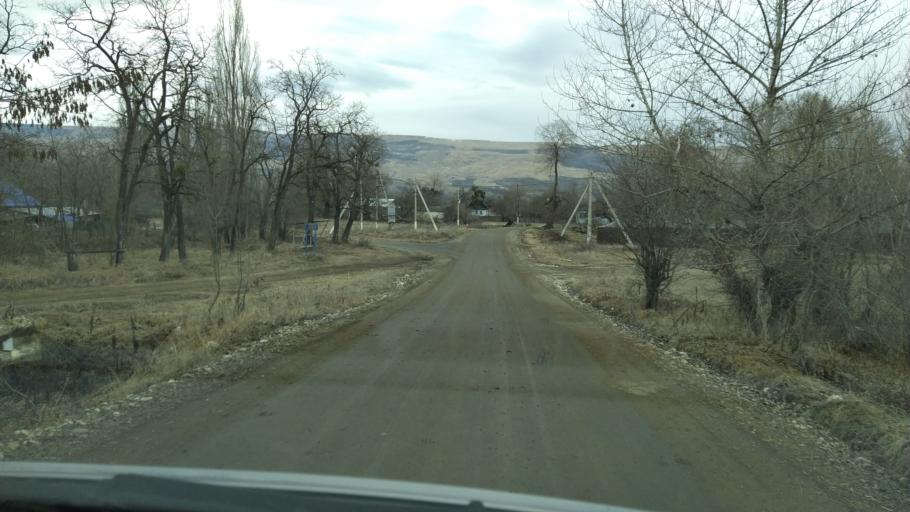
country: RU
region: Krasnodarskiy
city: Peredovaya
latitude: 44.0860
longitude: 41.3641
